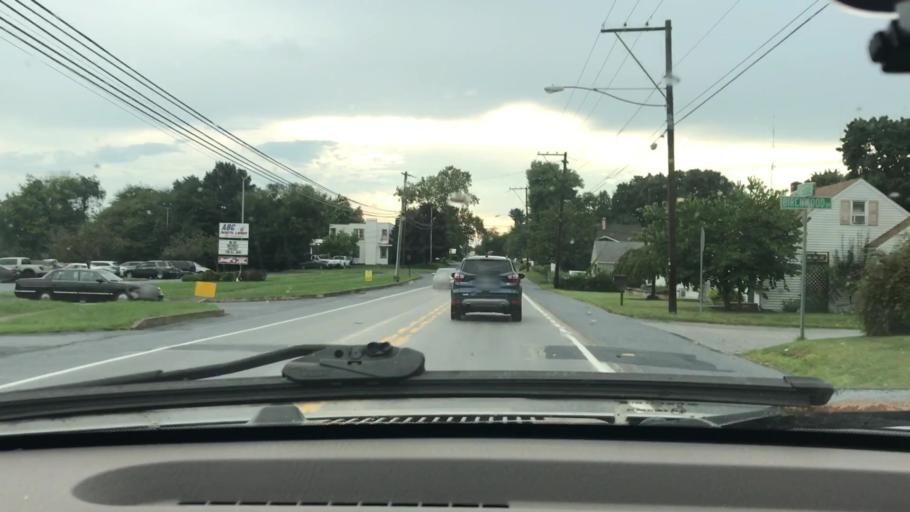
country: US
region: Pennsylvania
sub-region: Dauphin County
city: Colonial Park
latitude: 40.2931
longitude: -76.7979
